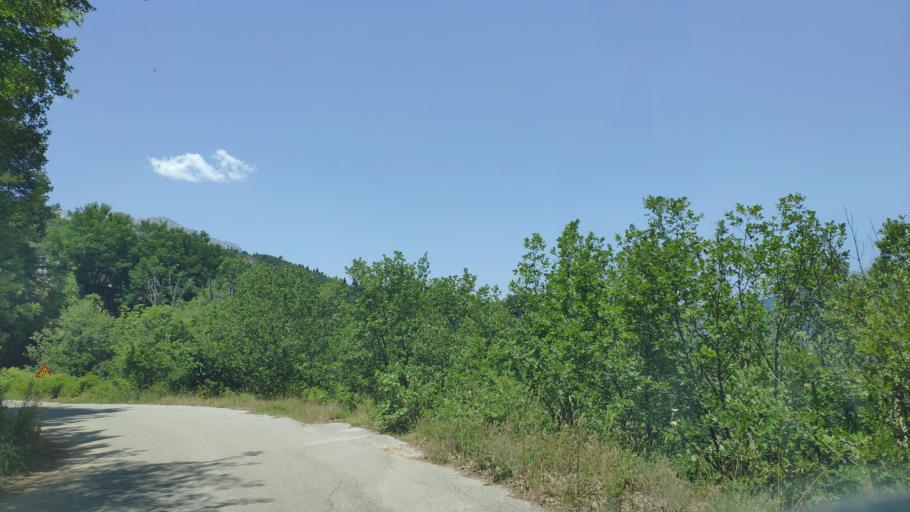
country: GR
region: Epirus
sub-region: Nomos Artas
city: Ano Kalentini
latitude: 39.1992
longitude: 21.3434
